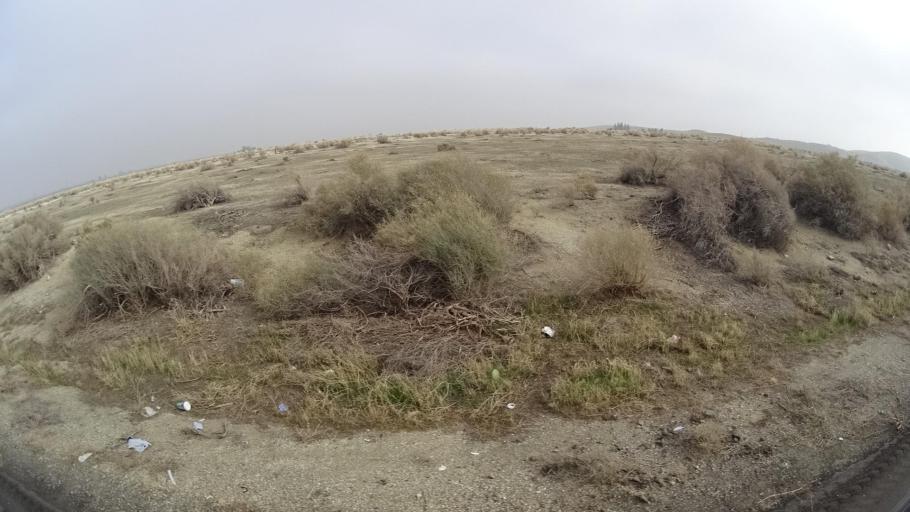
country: US
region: California
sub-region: Kern County
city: Maricopa
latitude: 35.0433
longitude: -119.3670
